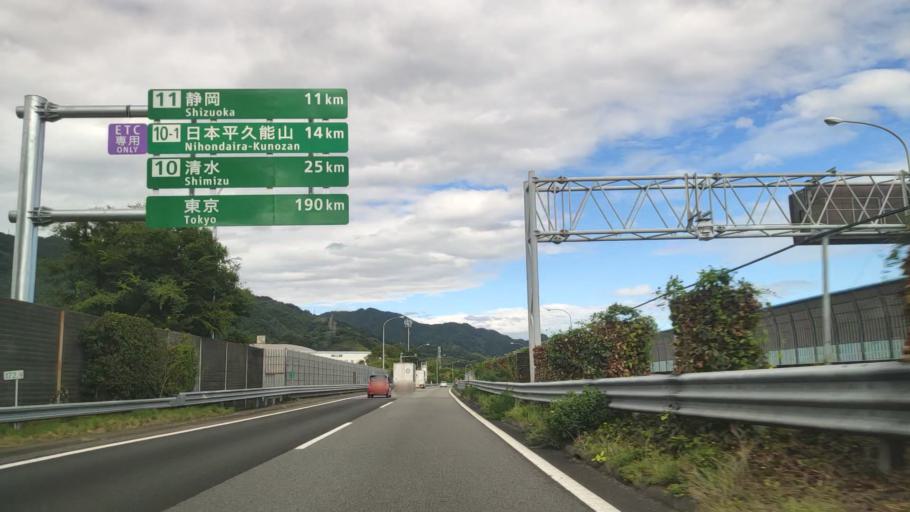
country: JP
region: Shizuoka
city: Yaizu
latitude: 34.8849
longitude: 138.3045
